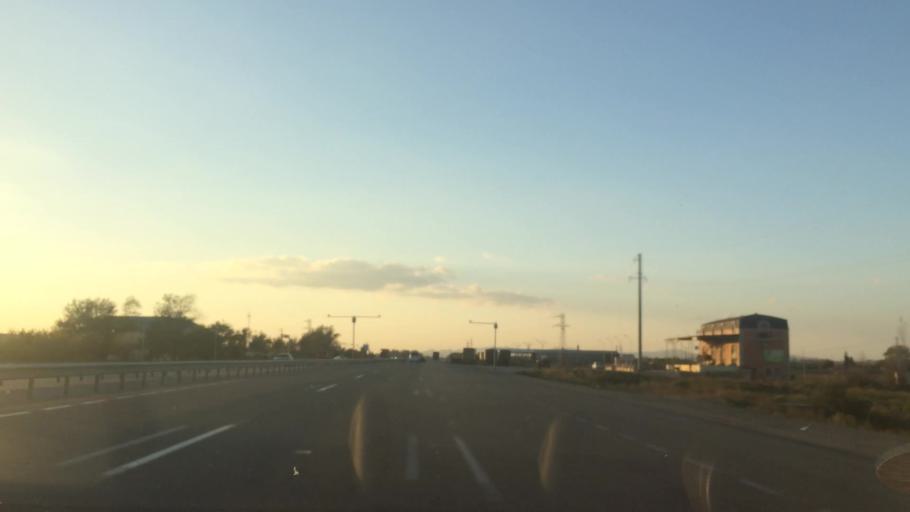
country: AZ
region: Haciqabul
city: Haciqabul
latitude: 40.0090
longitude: 49.1537
